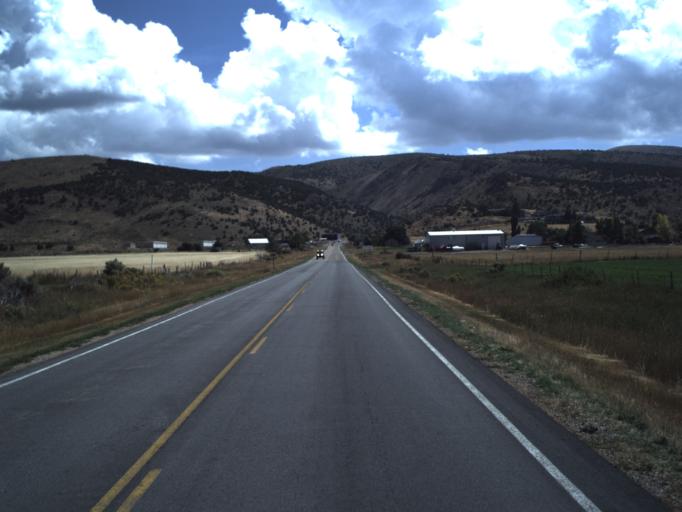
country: US
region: Utah
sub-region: Rich County
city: Randolph
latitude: 41.8309
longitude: -111.3210
